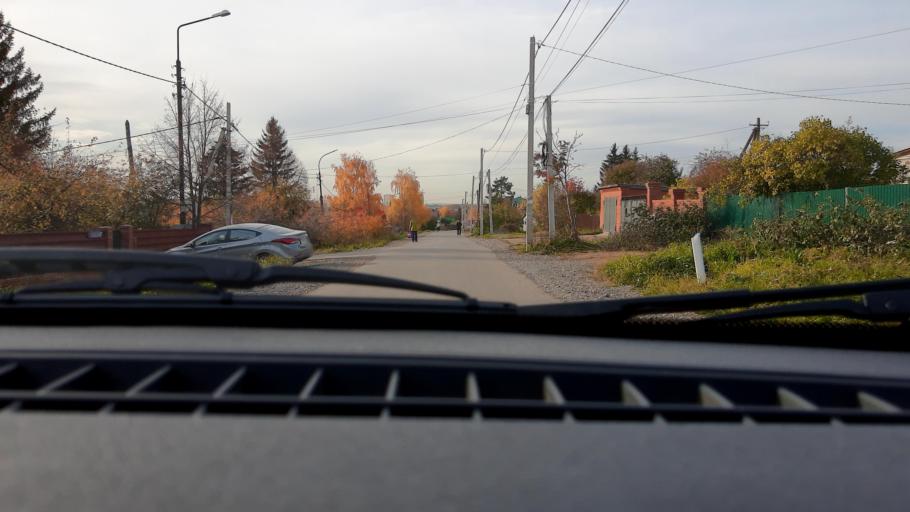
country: RU
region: Bashkortostan
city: Mikhaylovka
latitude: 54.8108
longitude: 55.8965
